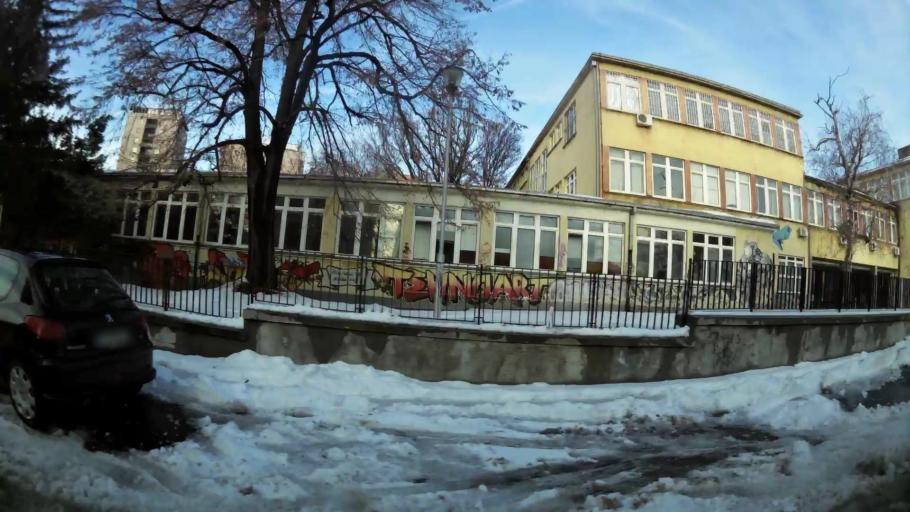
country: RS
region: Central Serbia
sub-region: Belgrade
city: Vracar
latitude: 44.8039
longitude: 20.4944
